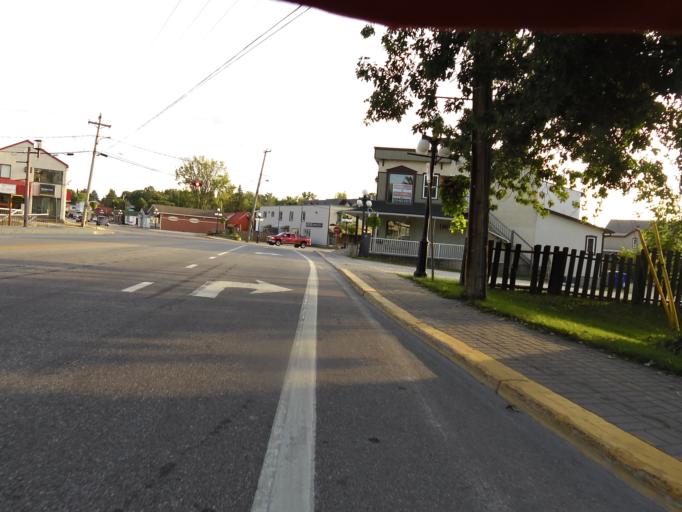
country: CA
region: Quebec
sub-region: Outaouais
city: Maniwaki
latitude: 46.3755
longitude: -75.9787
